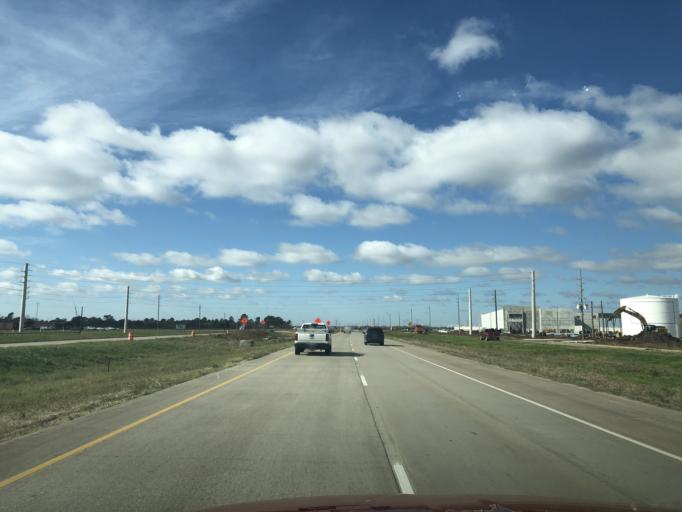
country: US
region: Texas
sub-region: Chambers County
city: Beach City
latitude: 29.7279
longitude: -94.9020
